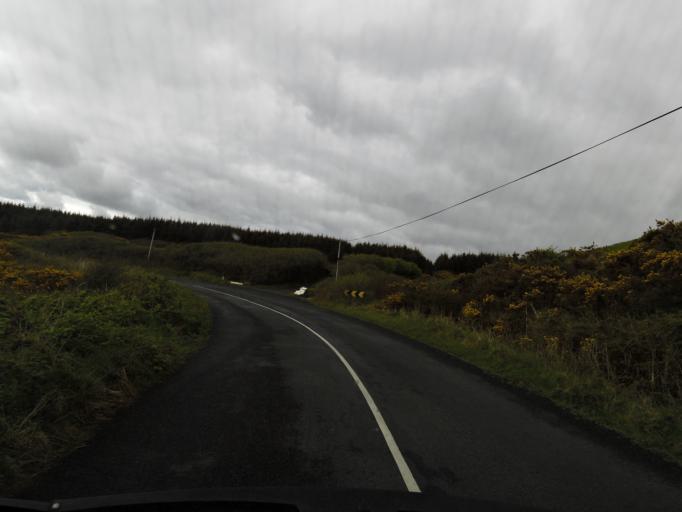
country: IE
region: Connaught
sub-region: County Galway
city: Bearna
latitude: 53.0420
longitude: -9.3369
